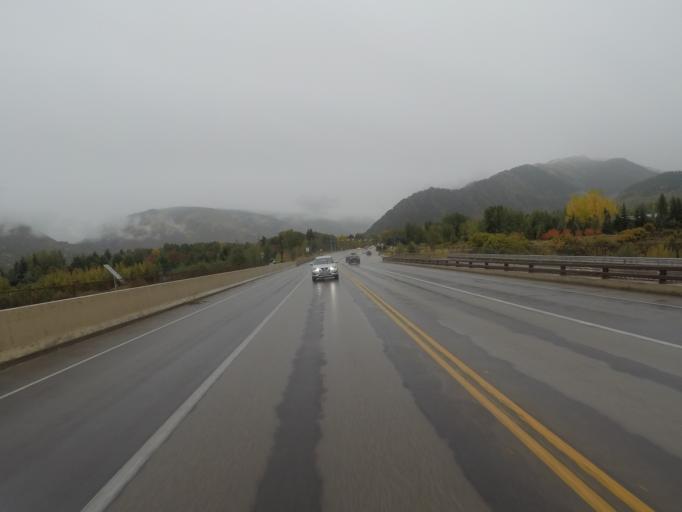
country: US
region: Colorado
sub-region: Pitkin County
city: Aspen
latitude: 39.2012
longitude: -106.8490
